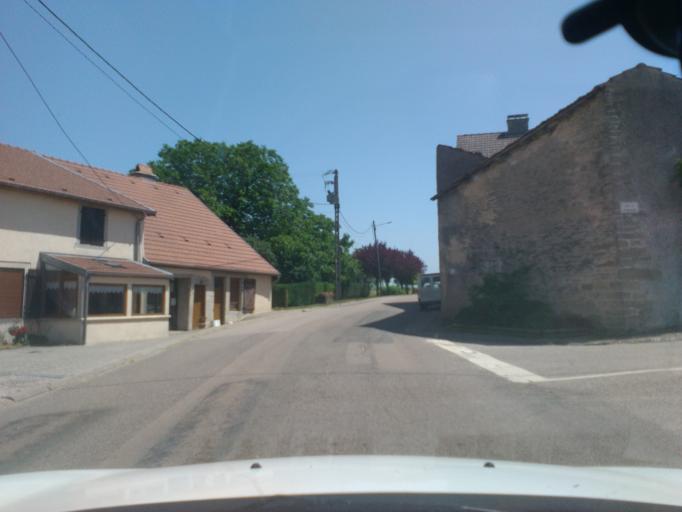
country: FR
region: Lorraine
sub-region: Departement des Vosges
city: Liffol-le-Grand
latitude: 48.4165
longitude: 5.5705
